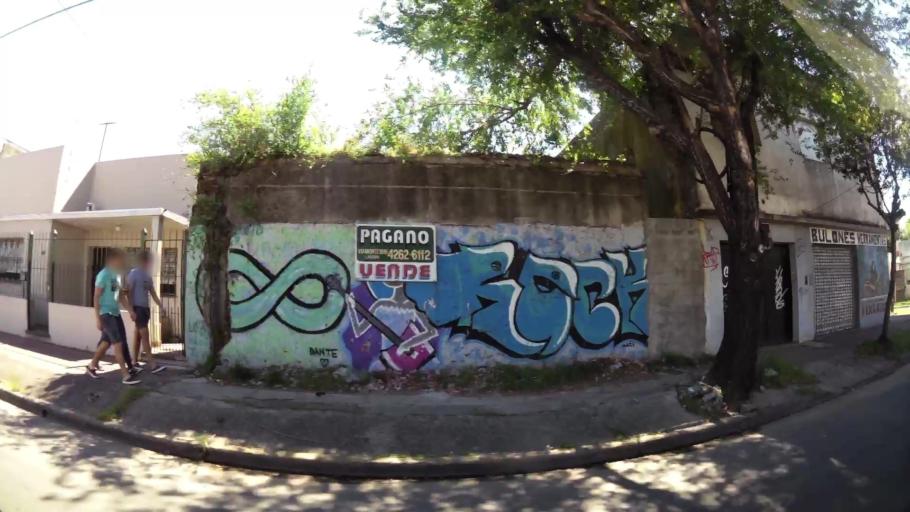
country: AR
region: Buenos Aires
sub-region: Partido de Lomas de Zamora
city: Lomas de Zamora
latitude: -34.7411
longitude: -58.4183
